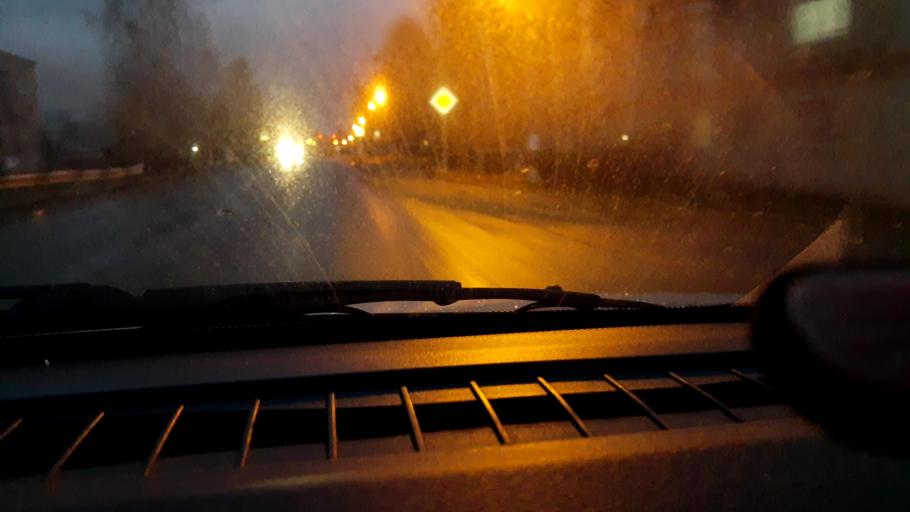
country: RU
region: Nizjnij Novgorod
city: Uren'
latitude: 57.4509
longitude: 45.7557
